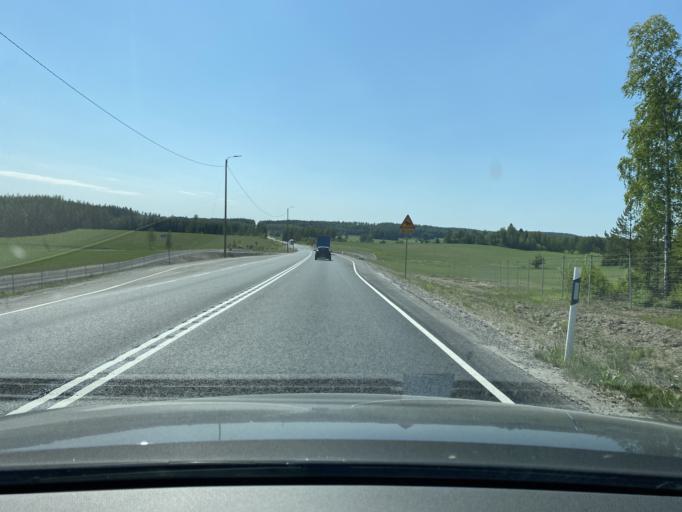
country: FI
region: Pirkanmaa
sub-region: Lounais-Pirkanmaa
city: Mouhijaervi
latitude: 61.3660
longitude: 23.1113
